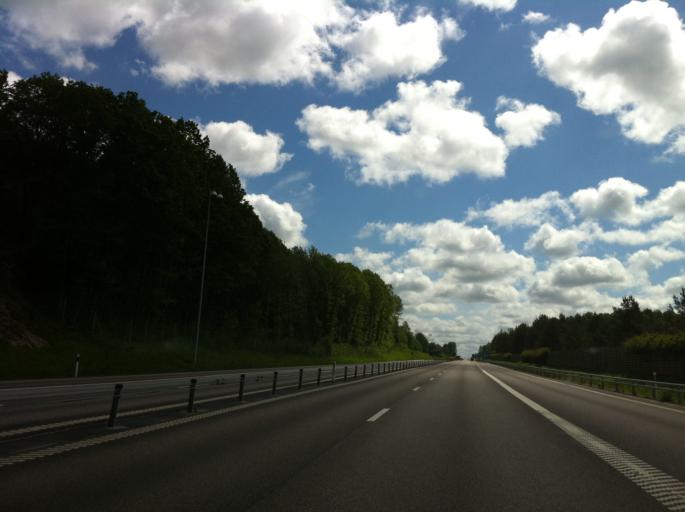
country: SE
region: Vaestra Goetaland
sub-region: Lilla Edets Kommun
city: Lilla Edet
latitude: 58.1446
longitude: 12.1353
